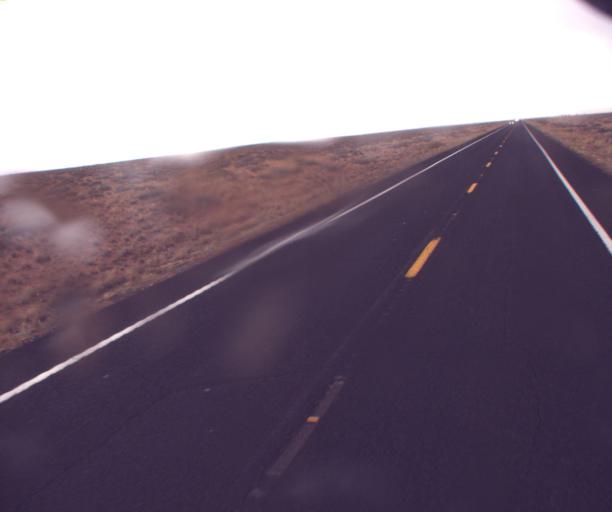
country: US
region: Arizona
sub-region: Coconino County
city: Tuba City
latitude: 36.1628
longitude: -111.1004
